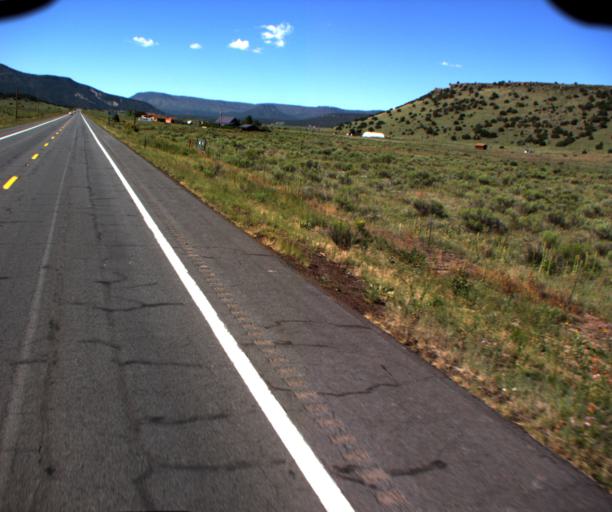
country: US
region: Arizona
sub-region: Apache County
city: Eagar
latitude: 34.0225
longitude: -109.1841
